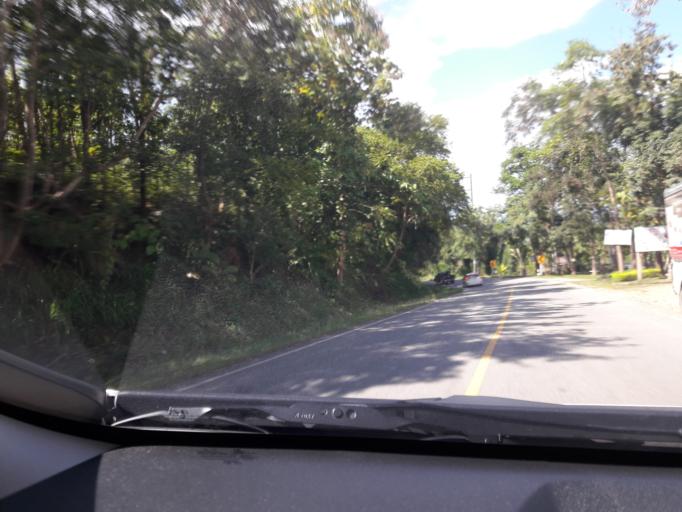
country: TH
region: Mae Hong Son
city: Mae Hi
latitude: 19.3110
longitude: 98.4530
